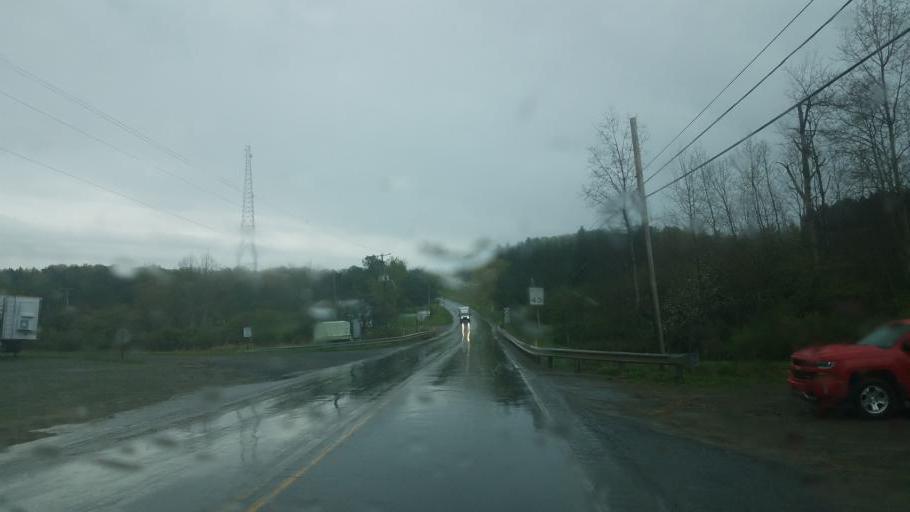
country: US
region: Pennsylvania
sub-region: Tioga County
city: Westfield
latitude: 41.9184
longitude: -77.7497
